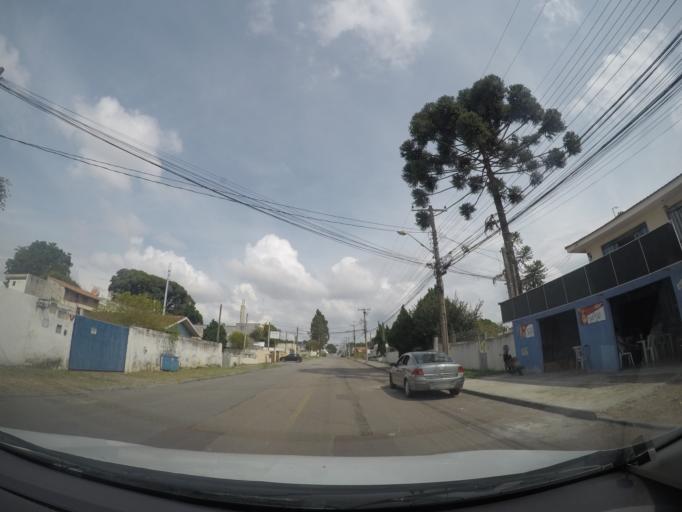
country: BR
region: Parana
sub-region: Curitiba
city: Curitiba
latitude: -25.4829
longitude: -49.2671
